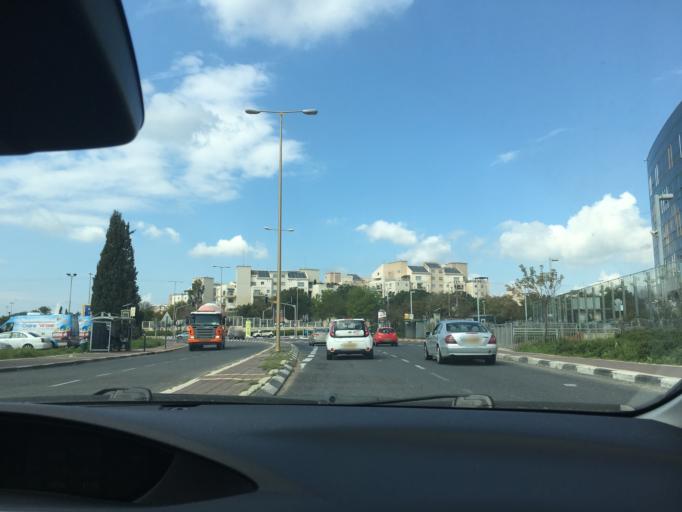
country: IL
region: Central District
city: Jaljulya
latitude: 32.1760
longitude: 34.9358
